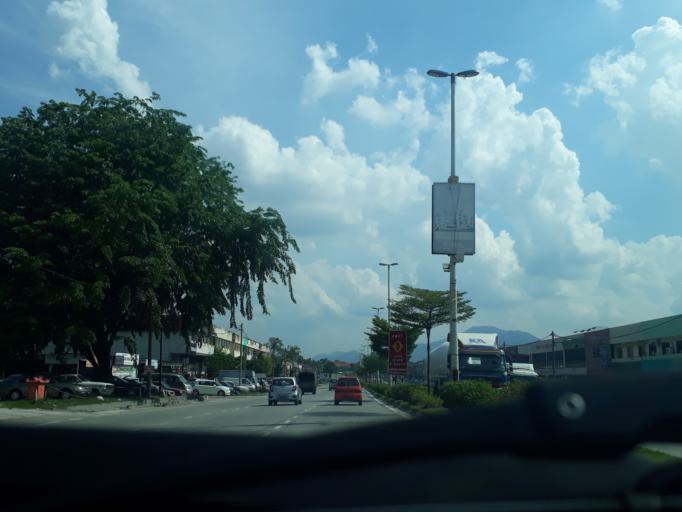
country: MY
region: Perak
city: Ipoh
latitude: 4.6438
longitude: 101.0976
